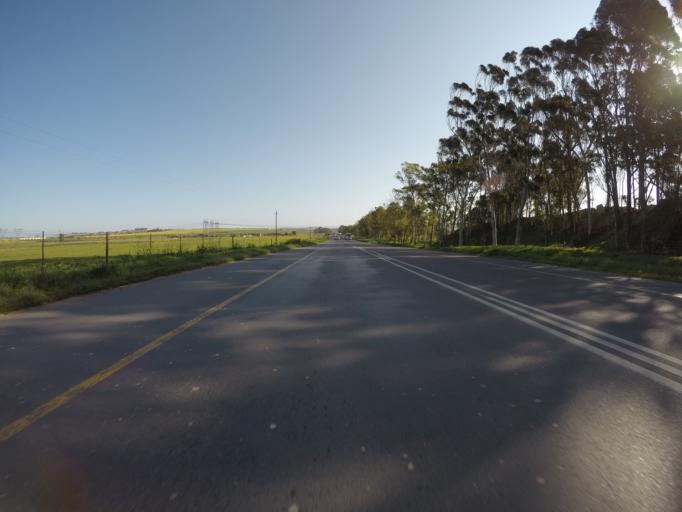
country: ZA
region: Western Cape
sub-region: City of Cape Town
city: Kraaifontein
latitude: -33.7965
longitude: 18.6918
